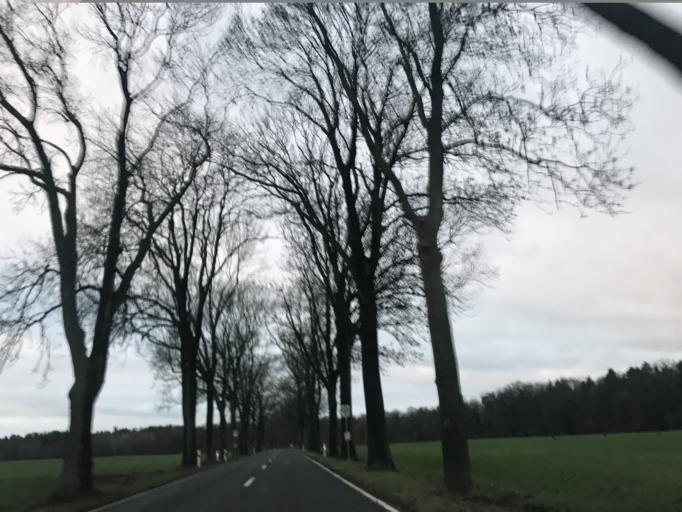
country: DE
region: Mecklenburg-Vorpommern
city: Rechlin
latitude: 53.1585
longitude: 12.7135
